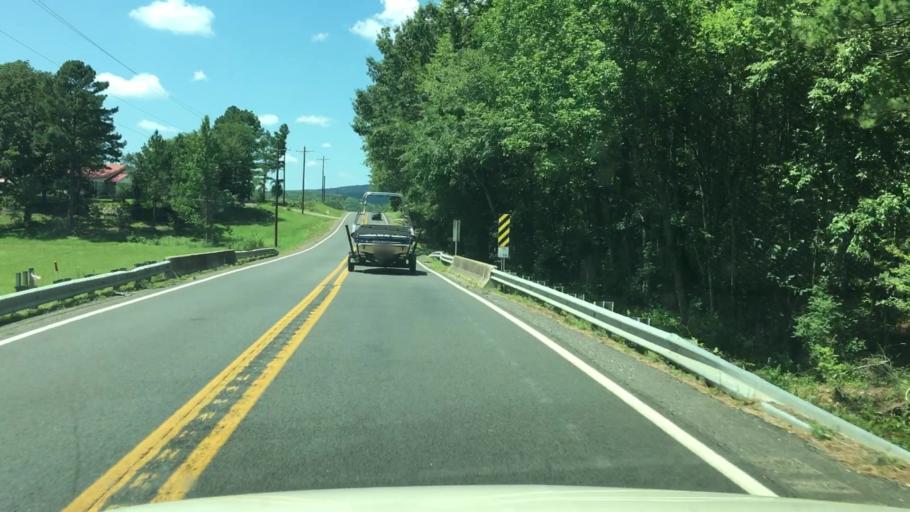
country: US
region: Arkansas
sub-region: Garland County
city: Lake Hamilton
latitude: 34.3304
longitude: -93.1747
